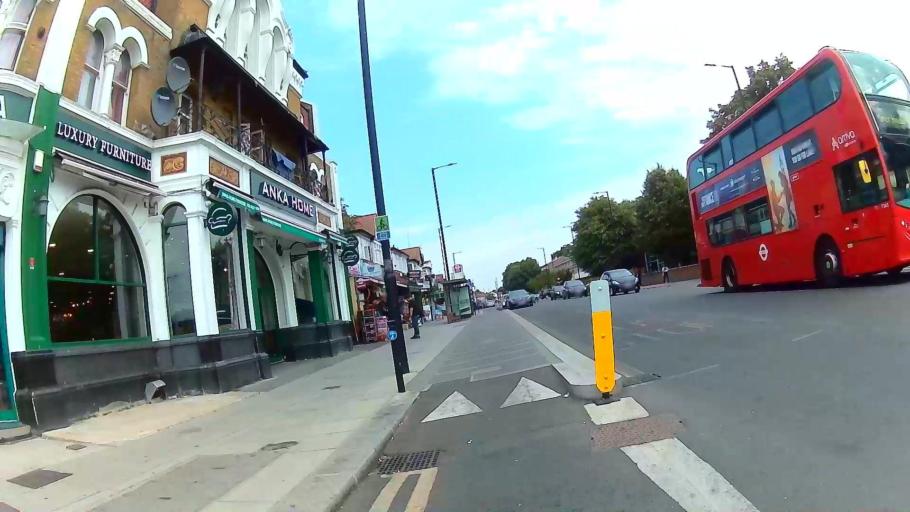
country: GB
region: England
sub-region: Greater London
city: Enfield
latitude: 51.6332
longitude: -0.0540
